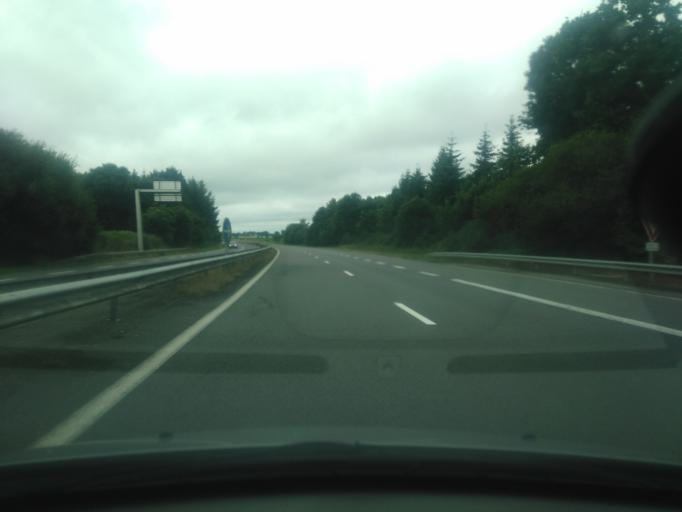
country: FR
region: Brittany
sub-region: Departement des Cotes-d'Armor
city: Plelan-le-Petit
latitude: 48.4268
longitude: -2.2228
